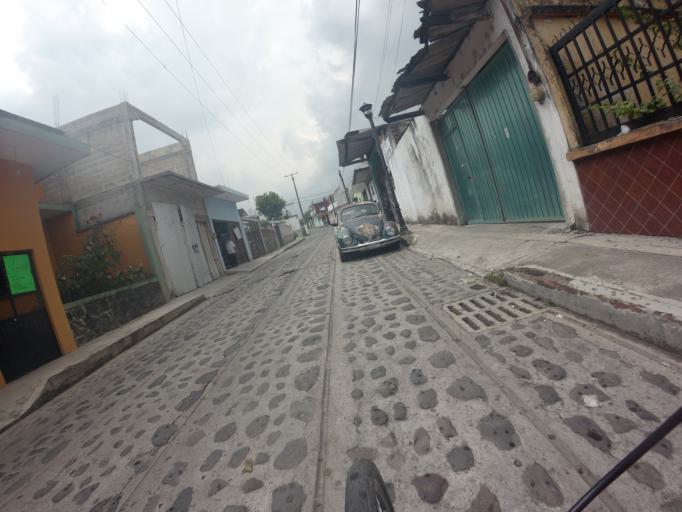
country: MX
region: Veracruz
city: Xico
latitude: 19.4192
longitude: -97.0033
